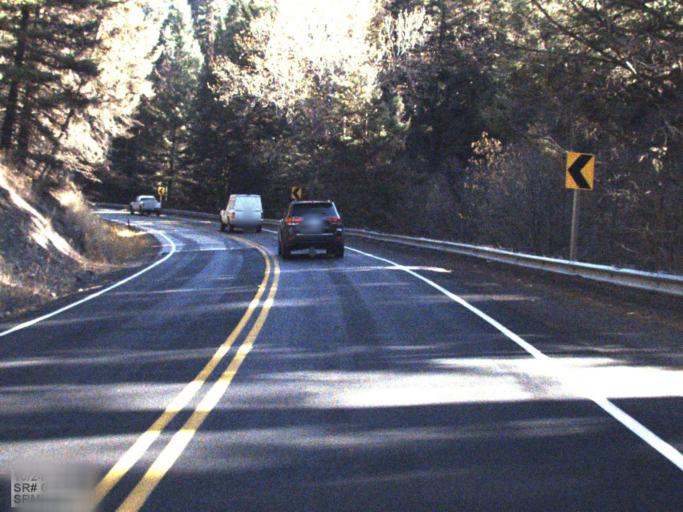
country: US
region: Washington
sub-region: Ferry County
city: Republic
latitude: 48.5959
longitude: -118.6329
